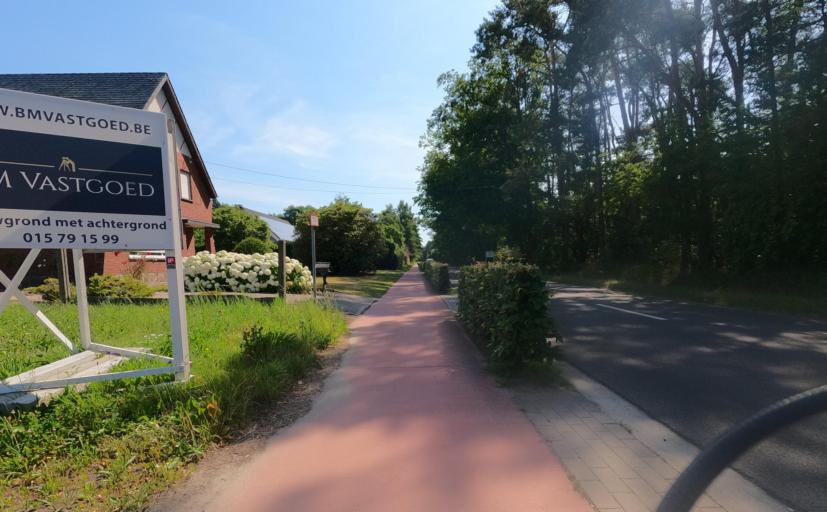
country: BE
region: Flanders
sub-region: Provincie Vlaams-Brabant
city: Keerbergen
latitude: 51.0156
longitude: 4.6080
